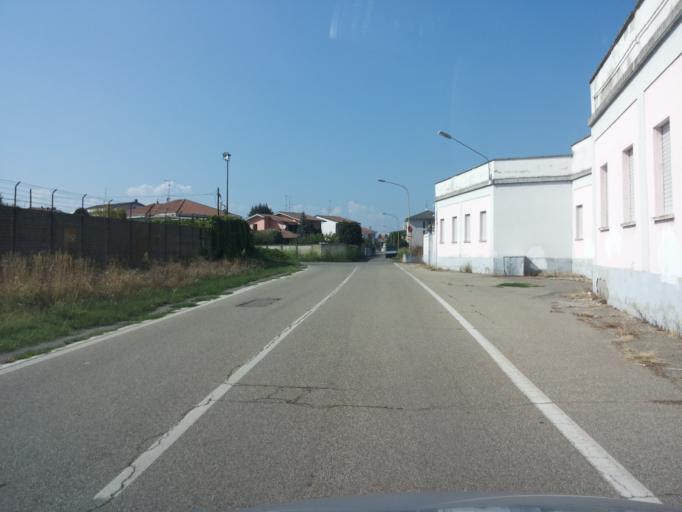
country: IT
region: Piedmont
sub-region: Provincia di Vercelli
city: Vercelli
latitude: 45.3109
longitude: 8.4322
